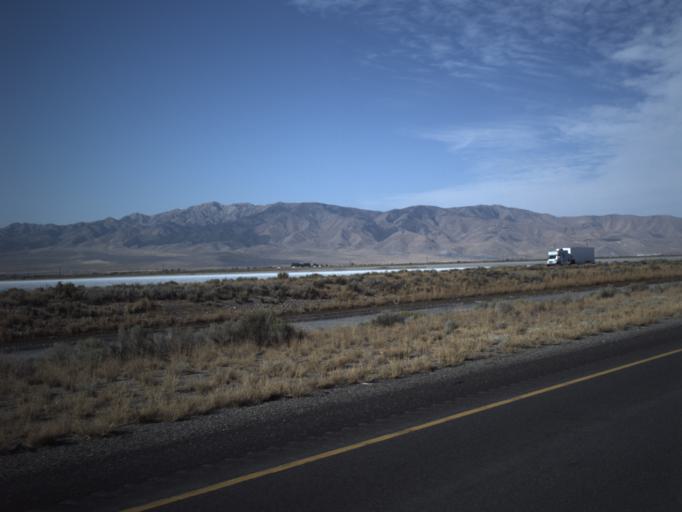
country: US
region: Utah
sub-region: Tooele County
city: Grantsville
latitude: 40.6757
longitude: -112.4011
